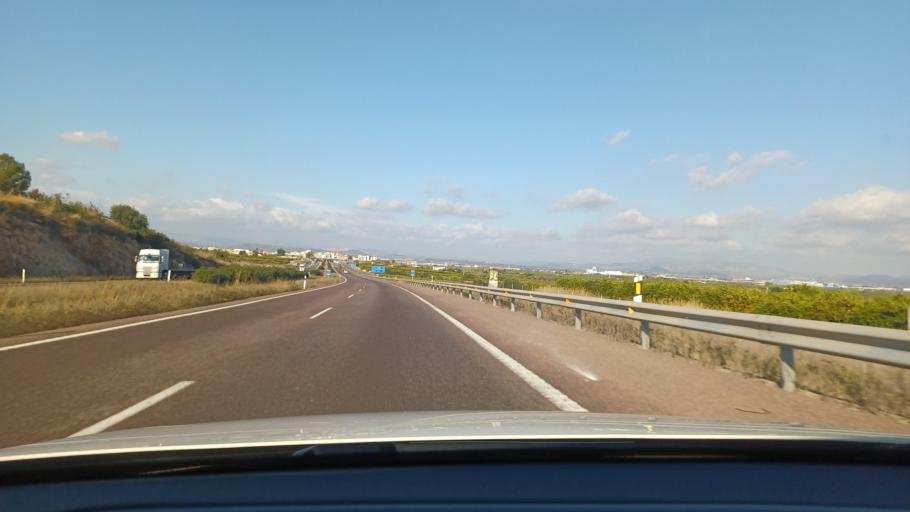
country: ES
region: Valencia
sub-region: Provincia de Castello
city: Betxi
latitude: 39.9074
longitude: -0.1954
